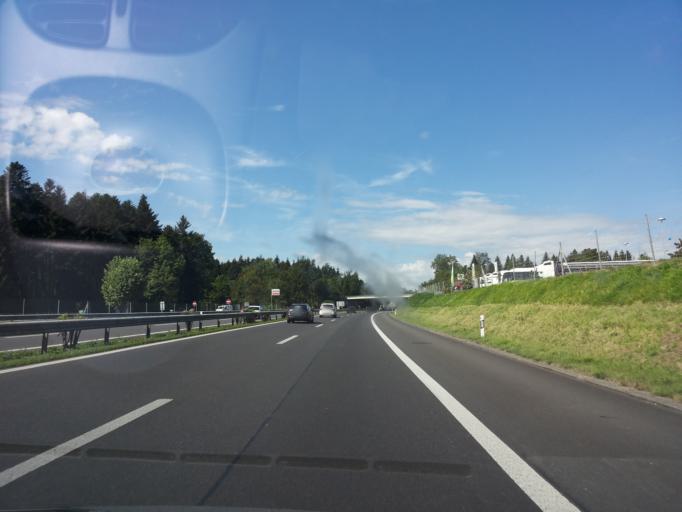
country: CH
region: Lucerne
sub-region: Sursee District
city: Neuenkirch
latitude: 47.1115
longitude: 8.2333
